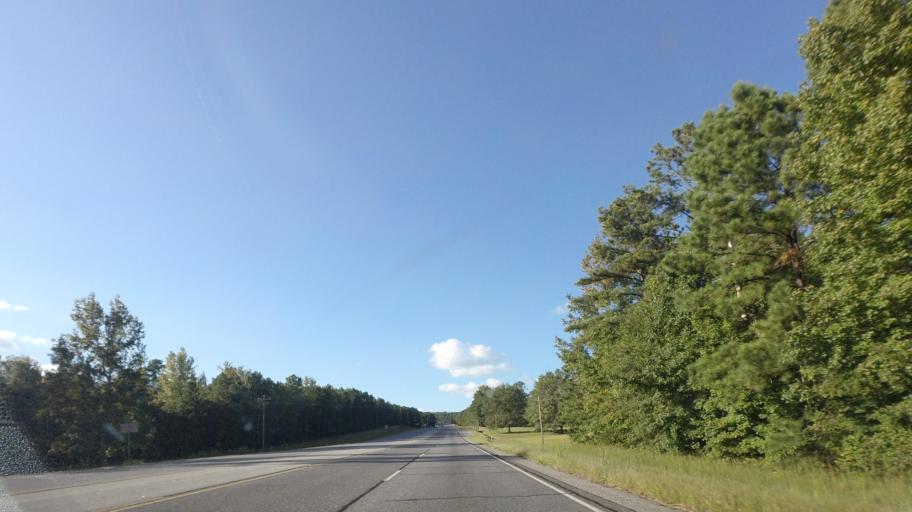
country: US
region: Georgia
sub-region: Upson County
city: Hannahs Mill
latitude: 32.9873
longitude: -84.3181
